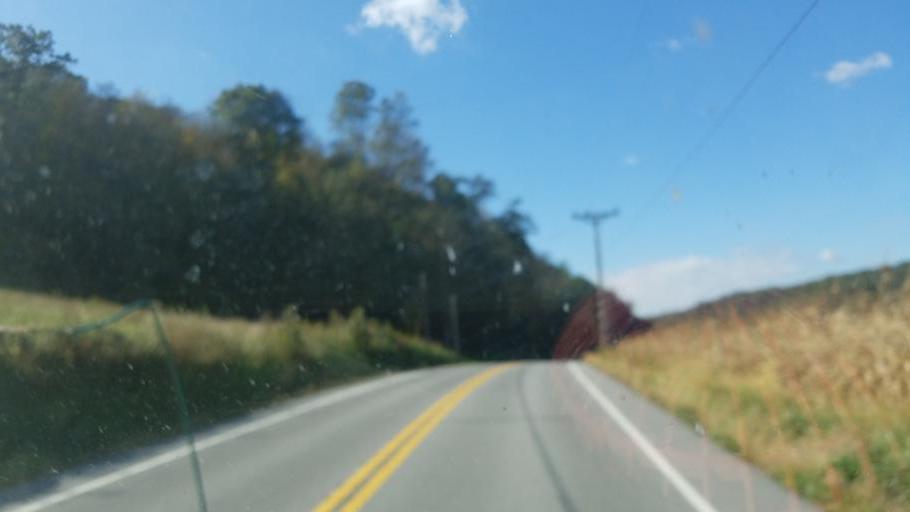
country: US
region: Pennsylvania
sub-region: Blair County
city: Claysburg
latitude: 40.1814
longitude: -78.5051
